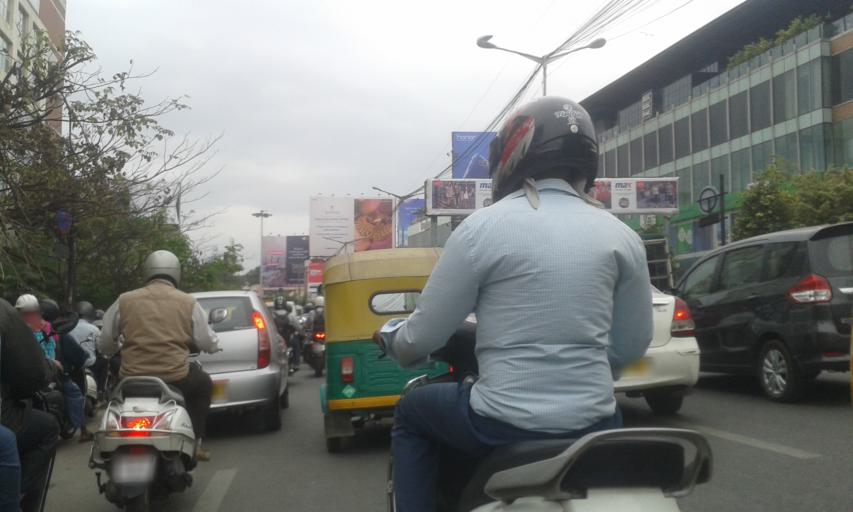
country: IN
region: Karnataka
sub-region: Bangalore Urban
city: Bangalore
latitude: 12.9349
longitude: 77.6199
